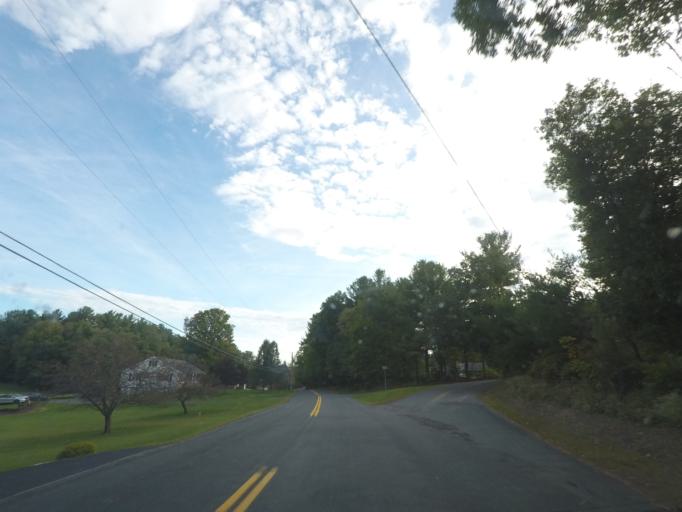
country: US
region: New York
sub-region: Rensselaer County
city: West Sand Lake
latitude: 42.6244
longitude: -73.6368
